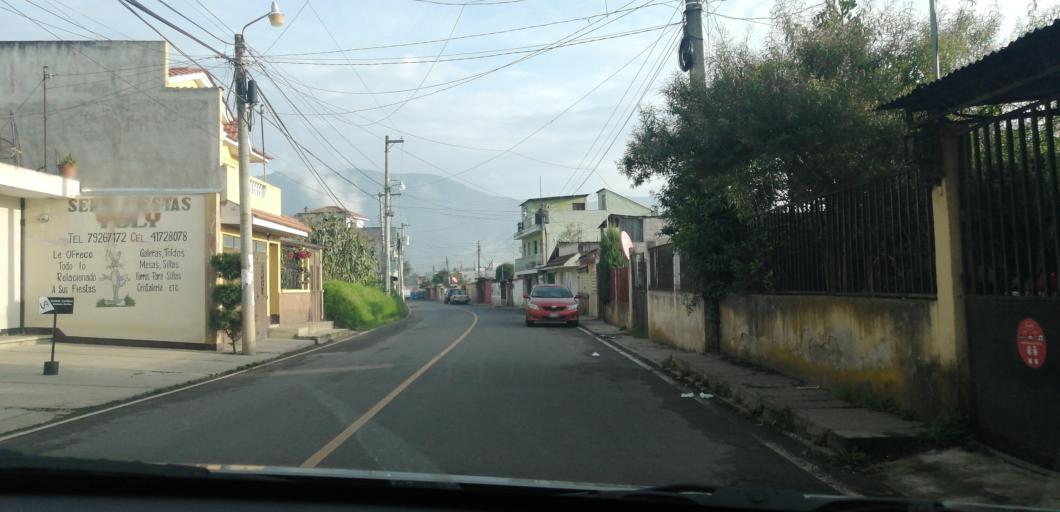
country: GT
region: Quetzaltenango
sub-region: Municipio de La Esperanza
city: La Esperanza
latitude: 14.8649
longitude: -91.5543
